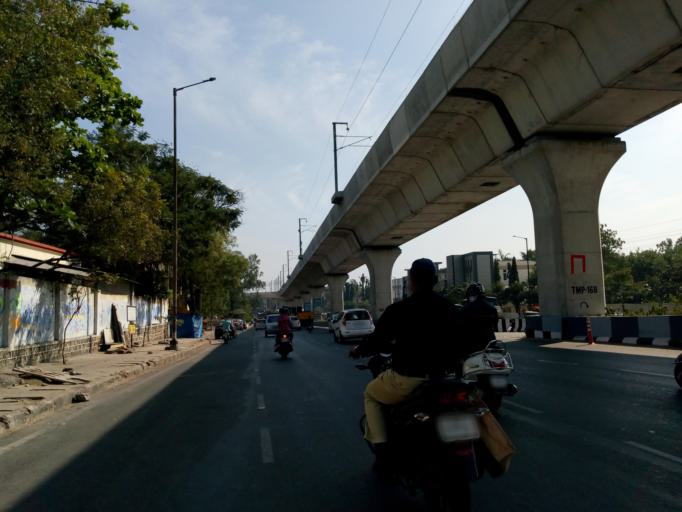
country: IN
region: Telangana
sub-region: Hyderabad
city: Malkajgiri
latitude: 17.4313
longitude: 78.5247
